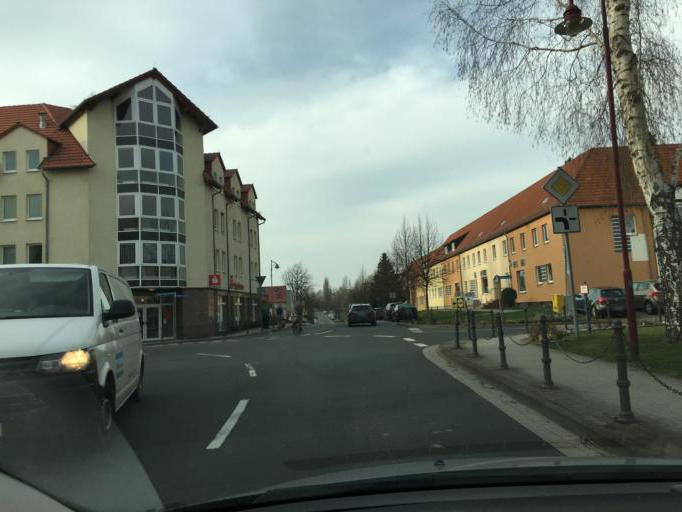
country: DE
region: Saxony
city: Kitzscher
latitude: 51.1642
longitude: 12.5538
